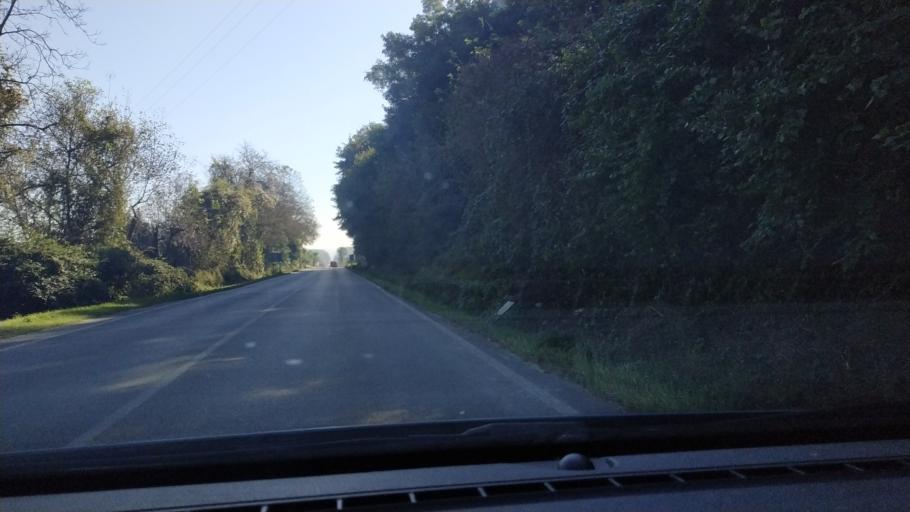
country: IT
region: Piedmont
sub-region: Provincia di Torino
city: San Sebastiano da Po
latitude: 45.1670
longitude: 7.9749
